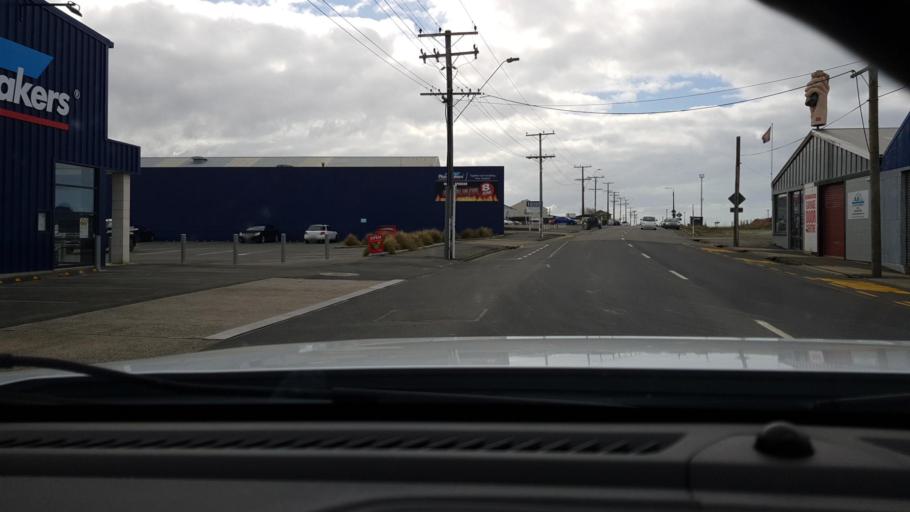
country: NZ
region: Otago
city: Oamaru
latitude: -45.1005
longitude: 170.9714
